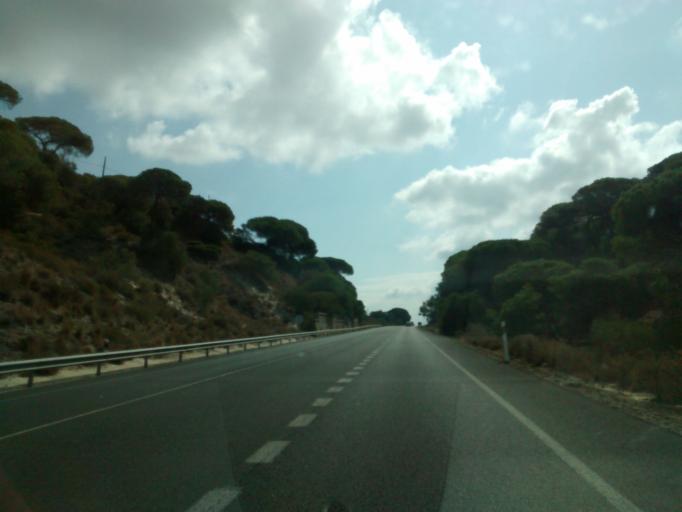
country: ES
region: Andalusia
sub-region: Provincia de Cadiz
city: Vejer de la Frontera
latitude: 36.2554
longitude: -5.9460
